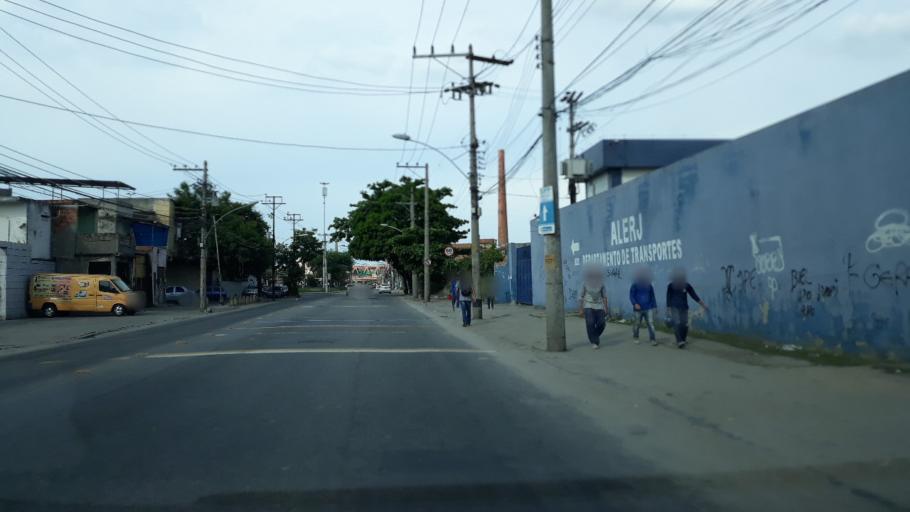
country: BR
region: Rio de Janeiro
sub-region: Rio De Janeiro
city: Rio de Janeiro
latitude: -22.8883
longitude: -43.2317
